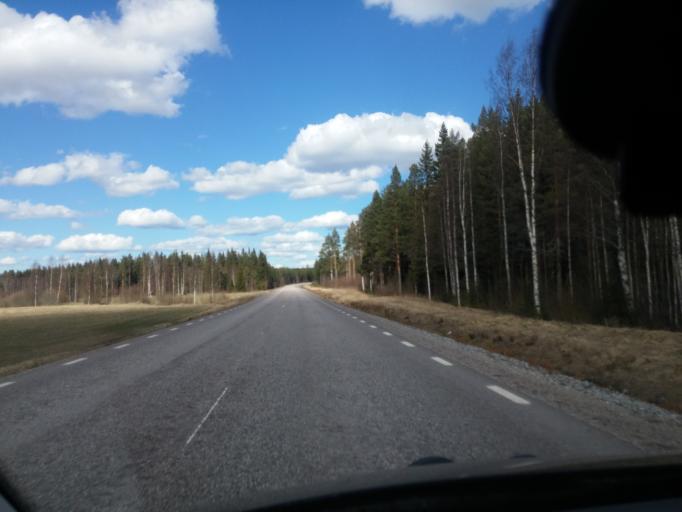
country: SE
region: Gaevleborg
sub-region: Ovanakers Kommun
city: Edsbyn
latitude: 61.2726
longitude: 15.8938
